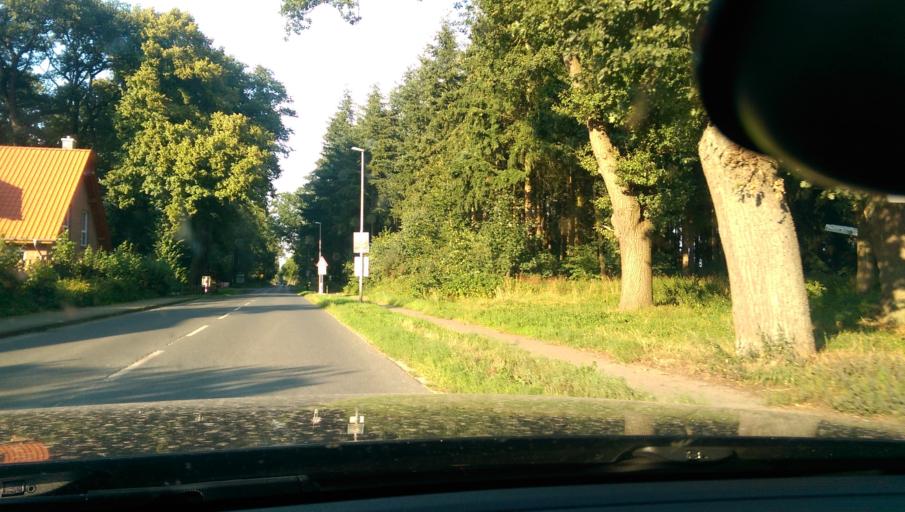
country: DE
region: Lower Saxony
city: Schwarmstedt
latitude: 52.5880
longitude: 9.5885
